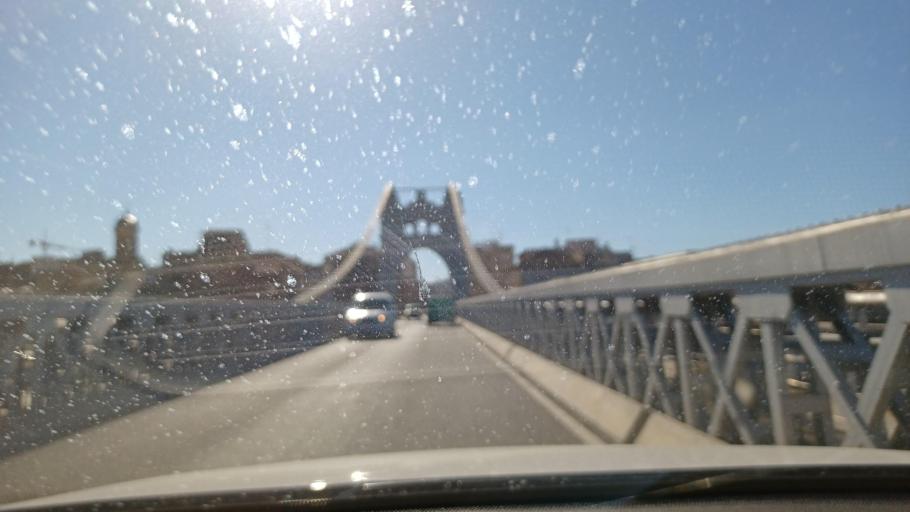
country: ES
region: Catalonia
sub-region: Provincia de Tarragona
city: Amposta
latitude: 40.7161
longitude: 0.5810
